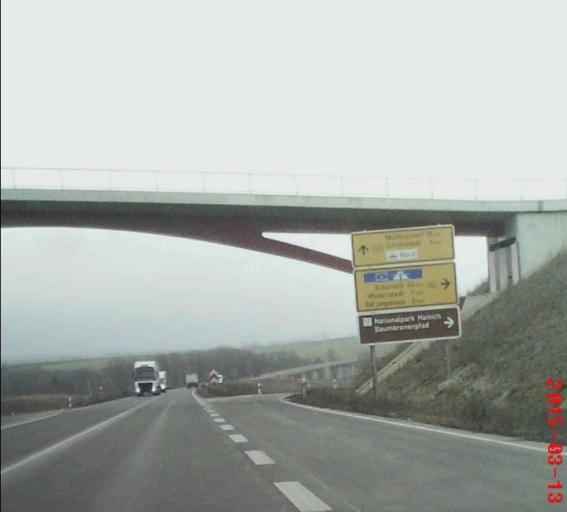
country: DE
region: Thuringia
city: Bad Langensalza
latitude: 51.0930
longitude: 10.6364
